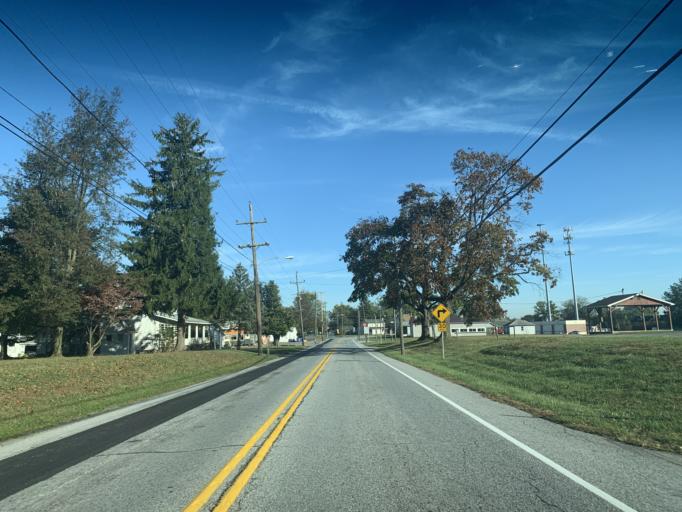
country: US
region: Pennsylvania
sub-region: Chester County
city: Parkesburg
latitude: 39.8888
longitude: -75.9229
